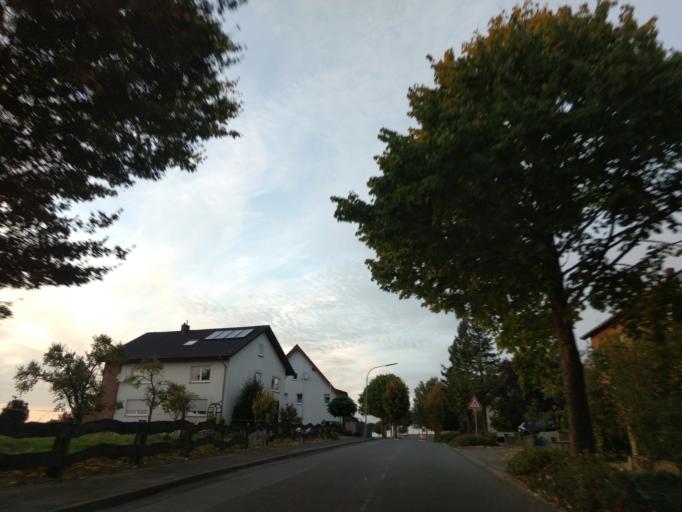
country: DE
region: North Rhine-Westphalia
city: Lichtenau
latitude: 51.6744
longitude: 8.8324
